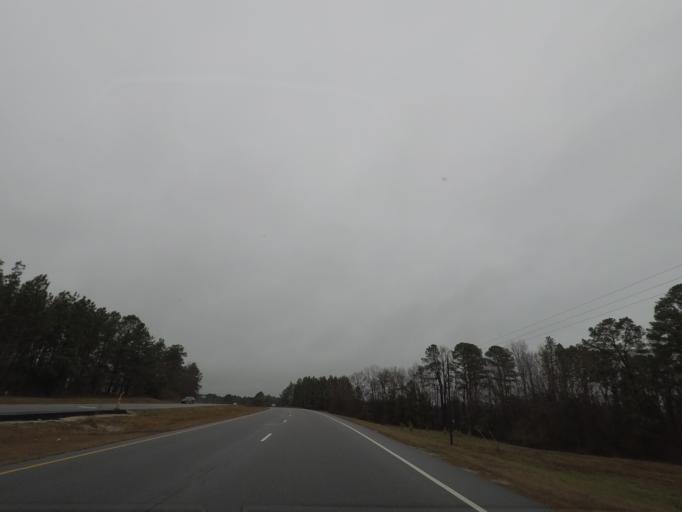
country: US
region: North Carolina
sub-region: Lee County
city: Broadway
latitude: 35.3332
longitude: -79.0944
